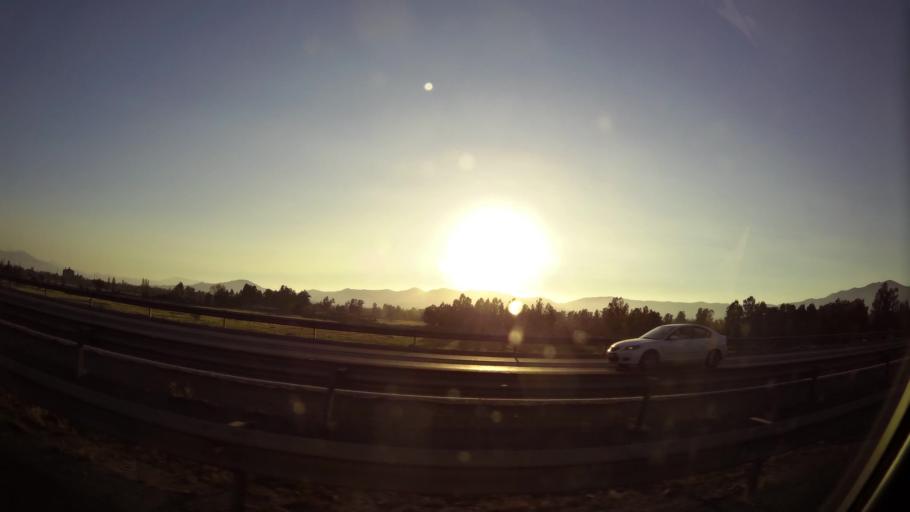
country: CL
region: Santiago Metropolitan
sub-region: Provincia de Talagante
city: Penaflor
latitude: -33.5914
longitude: -70.8445
